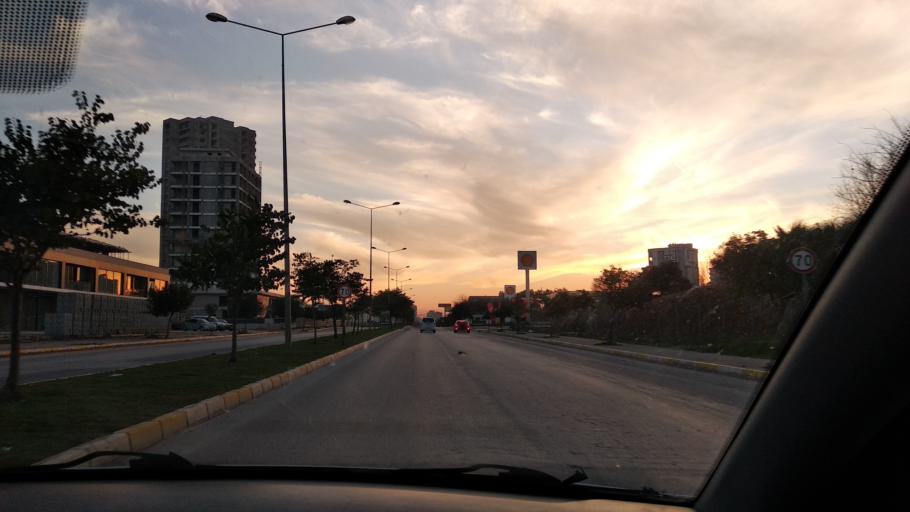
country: TR
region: Mersin
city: Mercin
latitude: 36.8004
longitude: 34.5819
